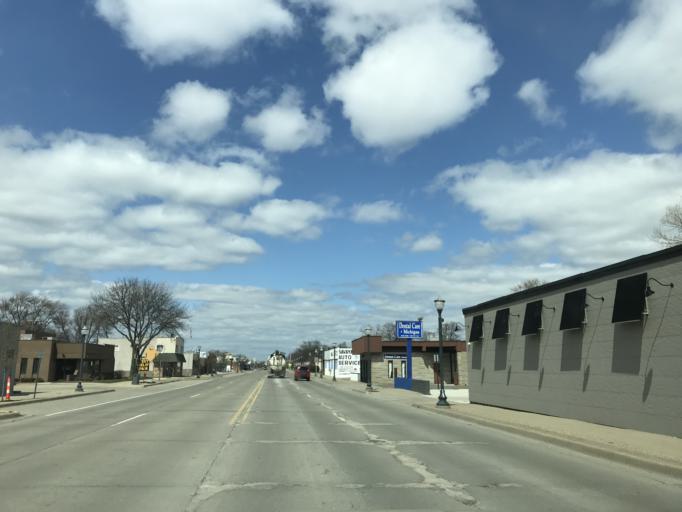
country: US
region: Michigan
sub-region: Oakland County
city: Hazel Park
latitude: 42.4651
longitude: -83.1041
